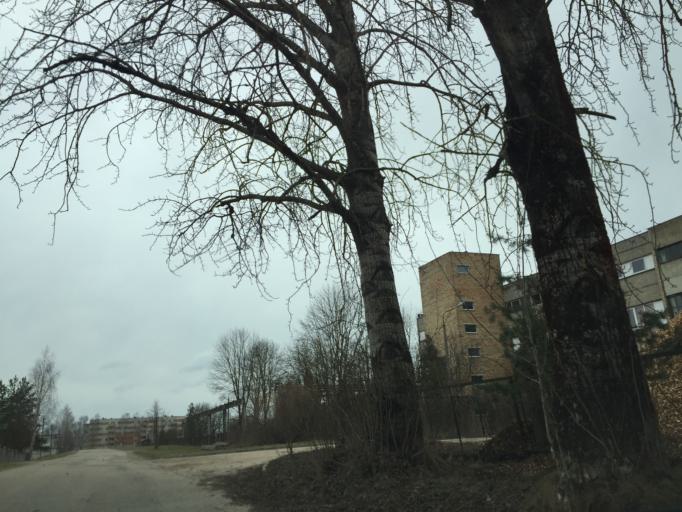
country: LV
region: Jekabpils Rajons
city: Jekabpils
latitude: 56.4900
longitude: 25.8955
